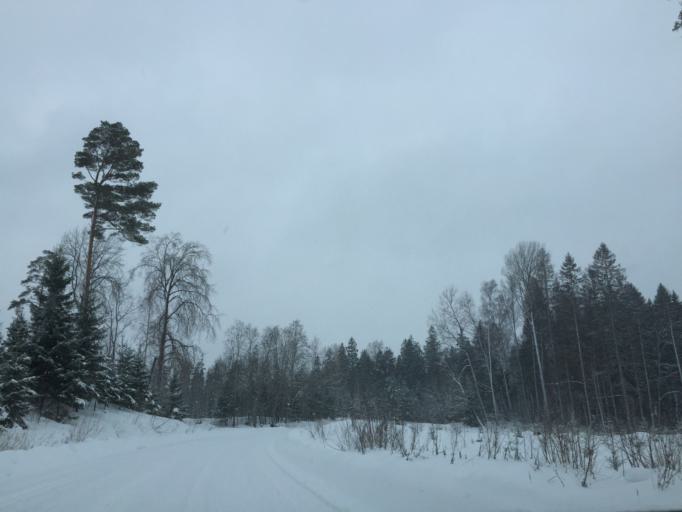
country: LV
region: Amatas Novads
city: Drabesi
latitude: 57.1642
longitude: 25.2889
